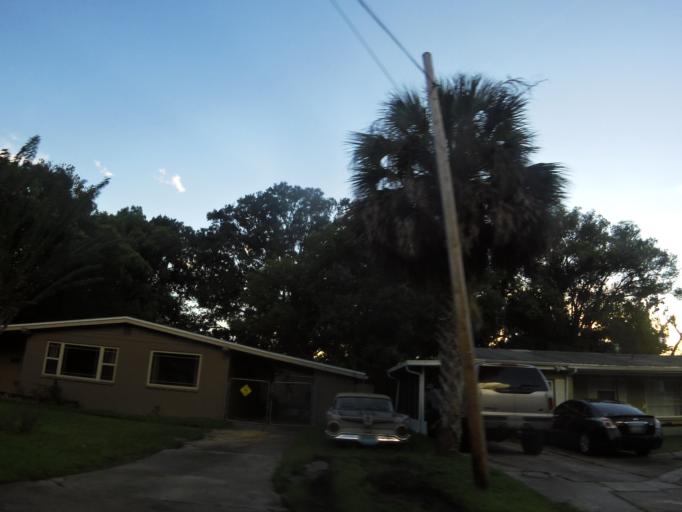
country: US
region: Florida
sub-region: Duval County
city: Jacksonville
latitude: 30.2340
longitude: -81.6077
